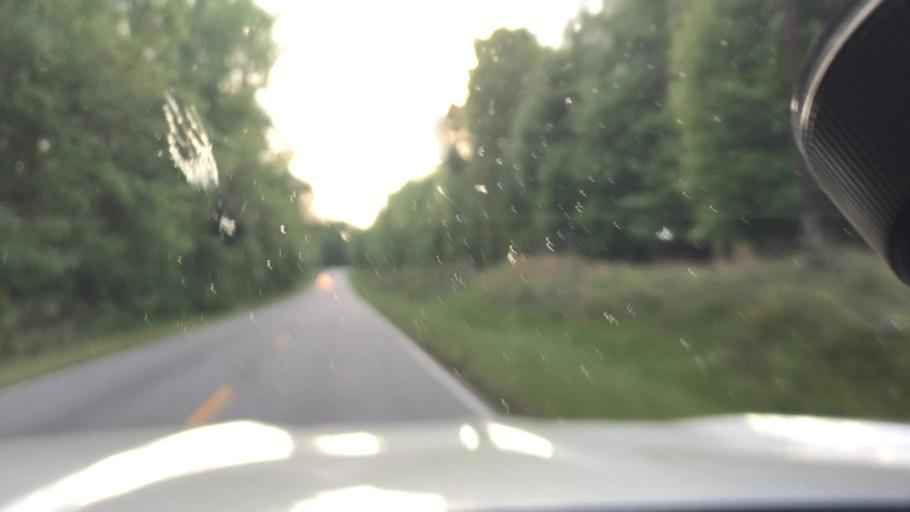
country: US
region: South Carolina
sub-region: Barnwell County
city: Blackville
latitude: 33.4734
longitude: -81.2024
